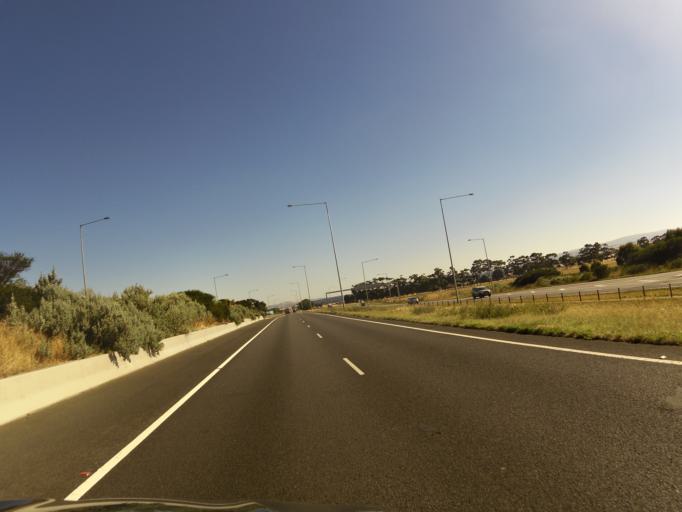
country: AU
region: Victoria
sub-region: Hume
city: Craigieburn
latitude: -37.5679
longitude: 144.9409
